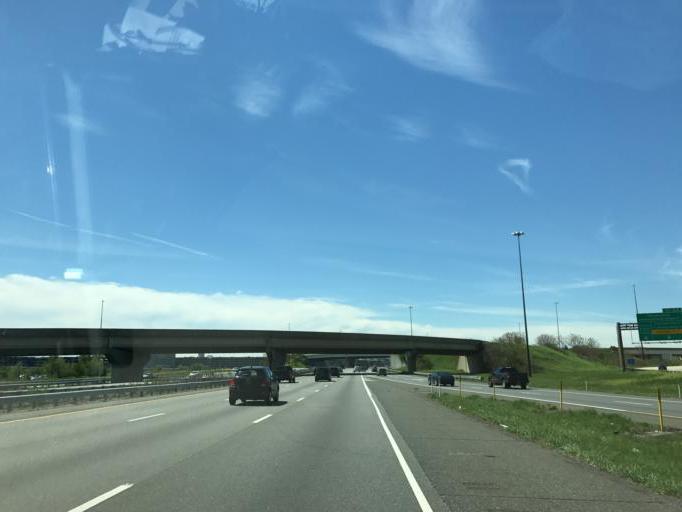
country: US
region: Pennsylvania
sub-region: Delaware County
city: Colwyn
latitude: 39.8852
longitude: -75.2439
